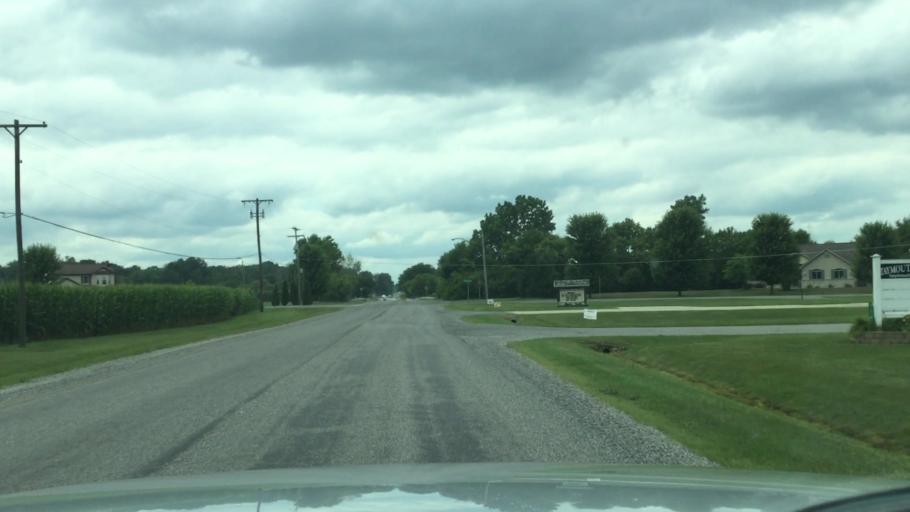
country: US
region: Michigan
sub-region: Saginaw County
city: Burt
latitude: 43.2500
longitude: -83.8665
